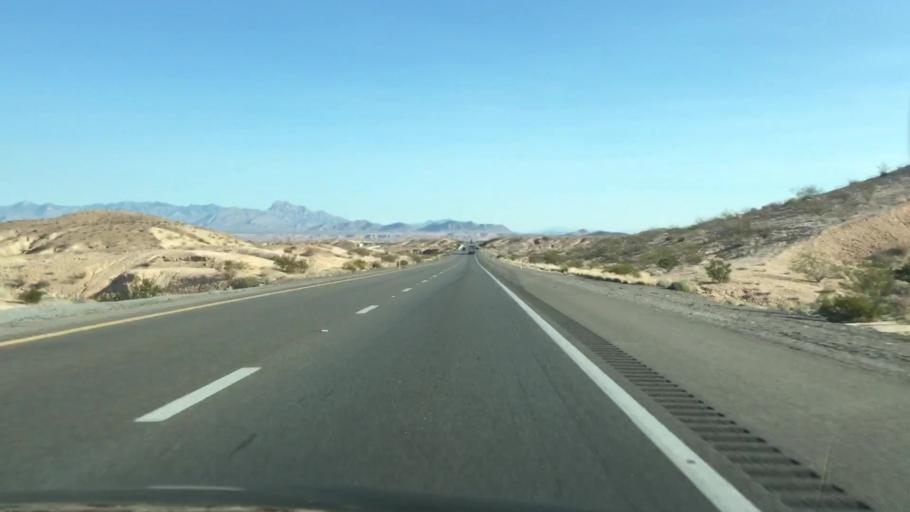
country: US
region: Nevada
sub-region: Clark County
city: Moapa Town
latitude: 36.6043
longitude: -114.6353
